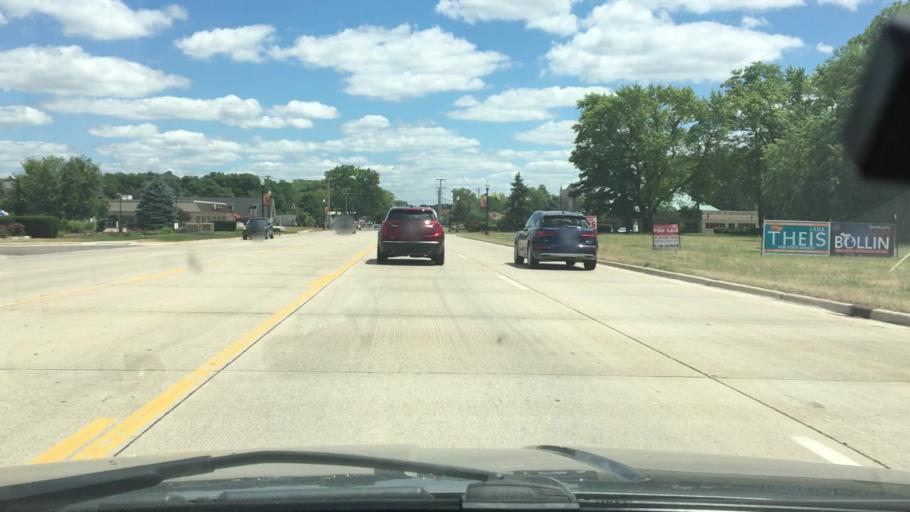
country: US
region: Michigan
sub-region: Livingston County
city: Brighton
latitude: 42.5184
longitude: -83.7471
